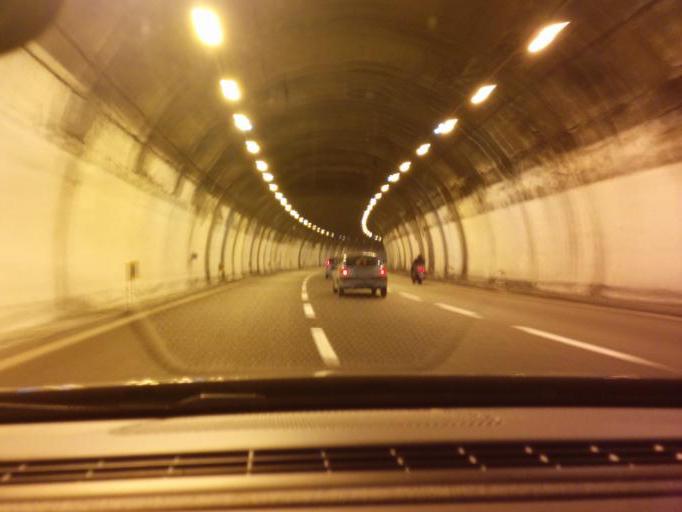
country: IT
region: Liguria
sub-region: Provincia di Genova
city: Mele
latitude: 44.4280
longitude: 8.7399
